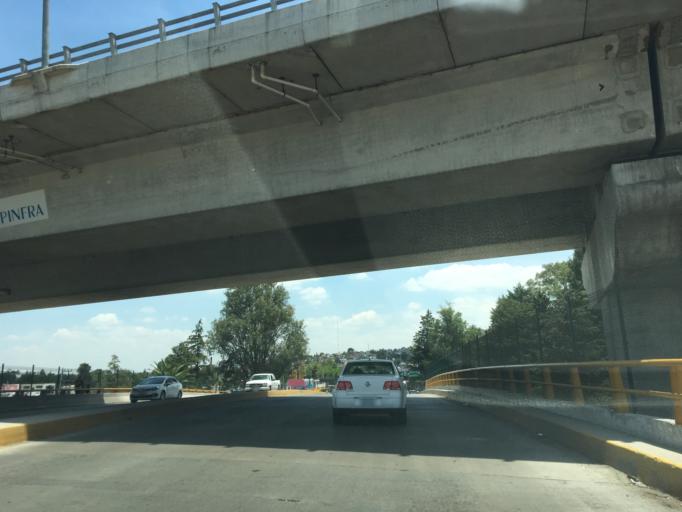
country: MX
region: Puebla
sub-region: Cuautlancingo
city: Sanctorum
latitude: 19.0971
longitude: -98.2299
